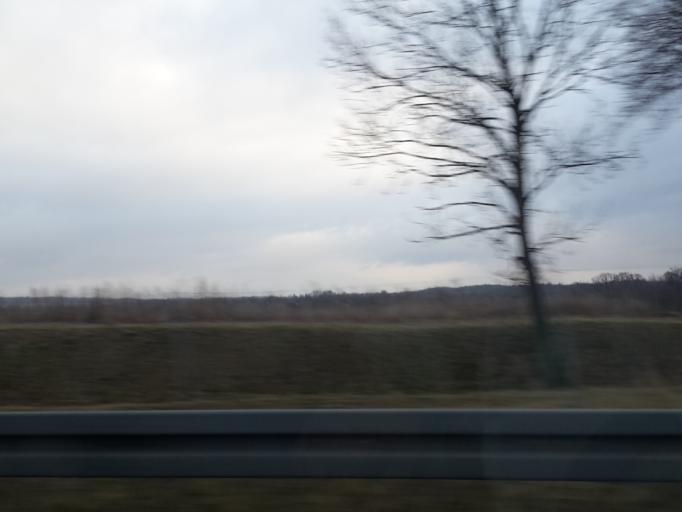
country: PL
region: Warmian-Masurian Voivodeship
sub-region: Powiat ostrodzki
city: Maldyty
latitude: 53.9340
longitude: 19.7054
